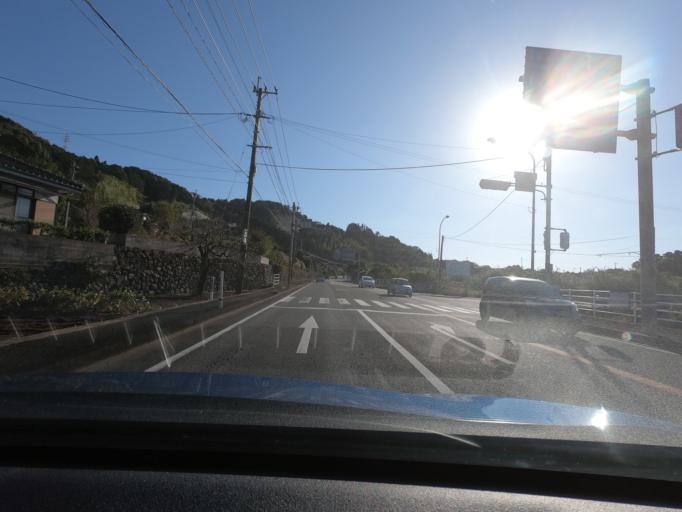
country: JP
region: Kagoshima
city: Izumi
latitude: 32.1513
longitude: 130.3642
